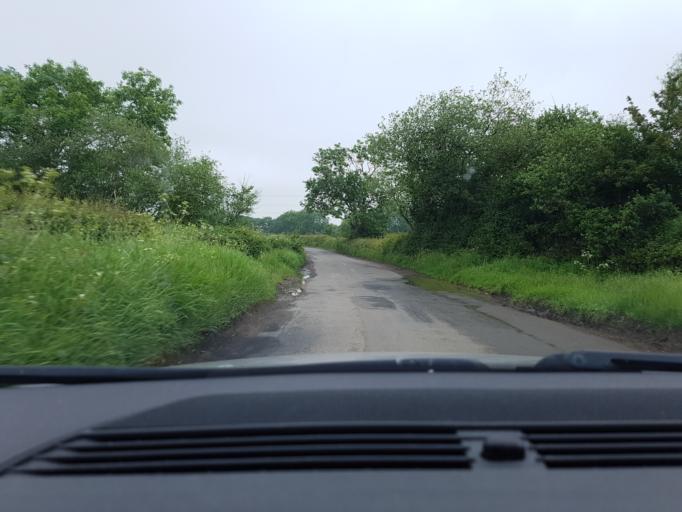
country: GB
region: England
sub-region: Buckinghamshire
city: Winslow
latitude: 51.9438
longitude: -0.8989
